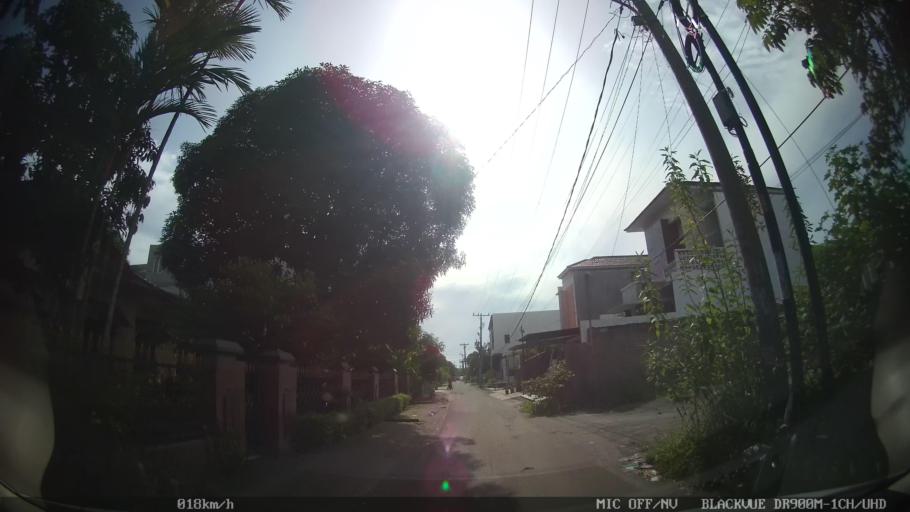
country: ID
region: North Sumatra
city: Medan
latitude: 3.6116
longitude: 98.6517
